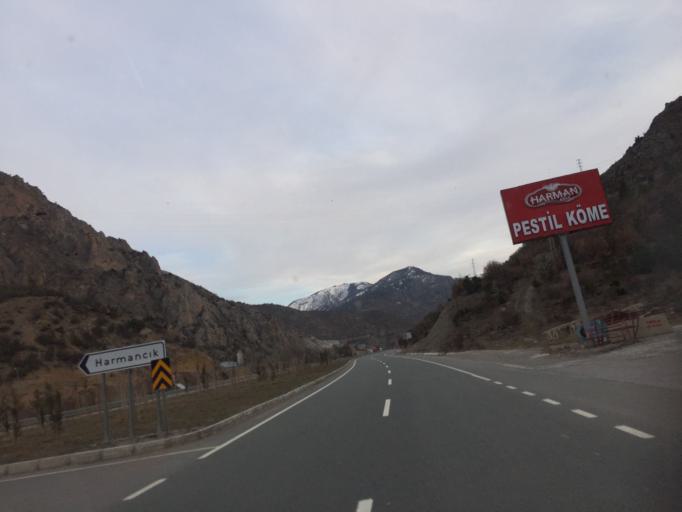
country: TR
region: Gumushane
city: Torul
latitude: 40.5340
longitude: 39.3329
